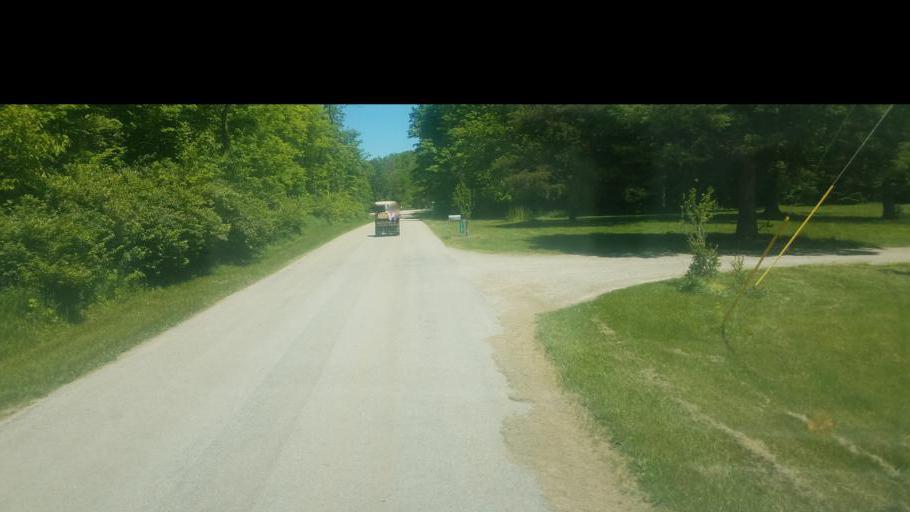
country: US
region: Ohio
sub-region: Miami County
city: Piqua
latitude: 40.2160
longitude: -84.2597
